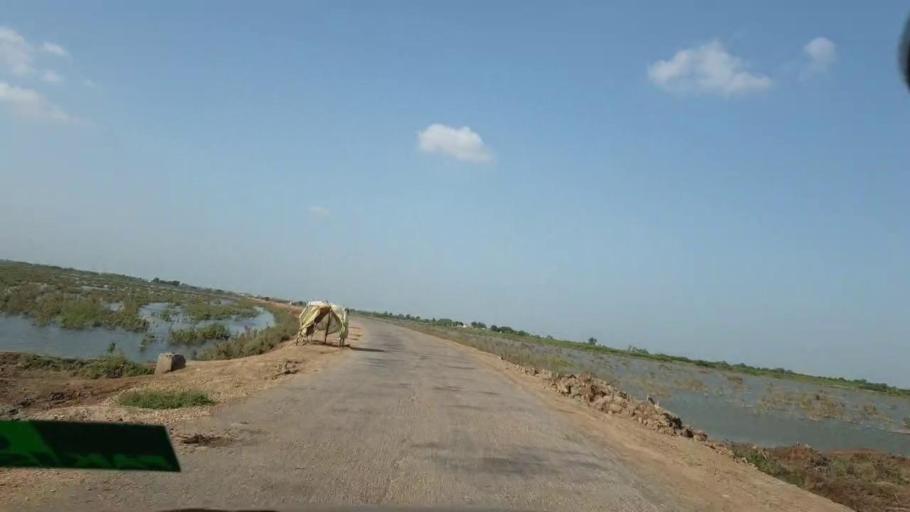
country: PK
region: Sindh
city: Tando Bago
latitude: 24.7288
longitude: 69.1987
